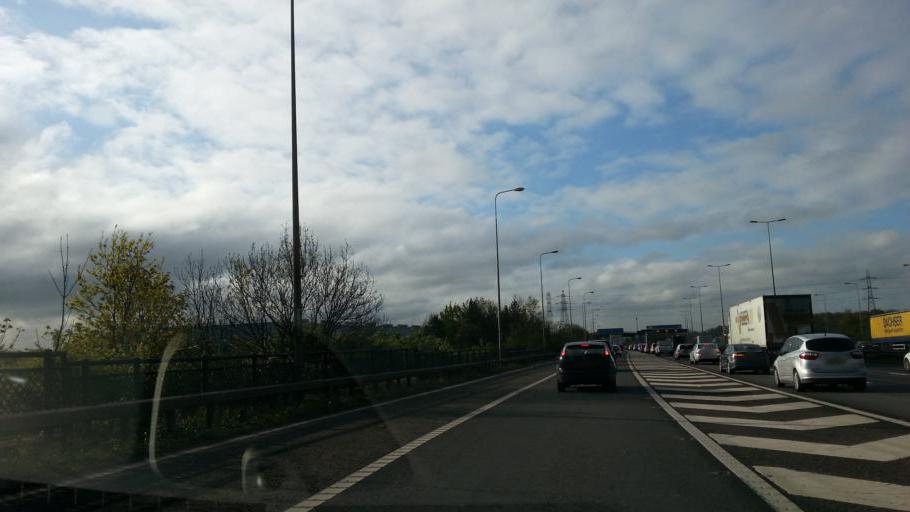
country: GB
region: England
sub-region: Leicestershire
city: Enderby
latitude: 52.6060
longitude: -1.1964
